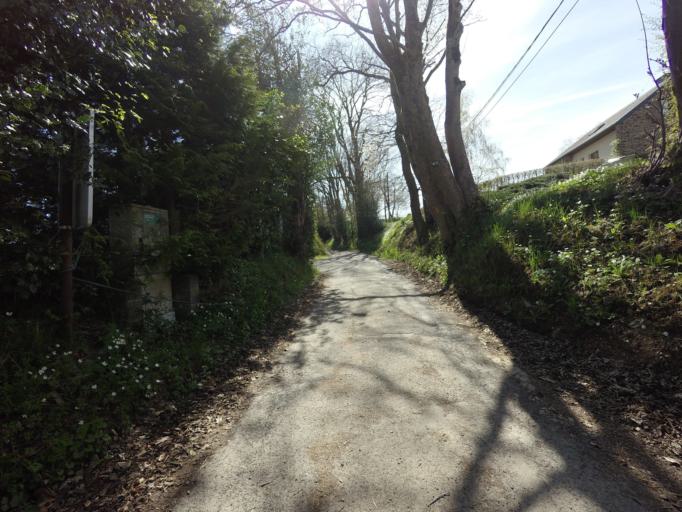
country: BE
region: Wallonia
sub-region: Province de Liege
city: Trois-Ponts
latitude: 50.4202
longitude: 5.8830
